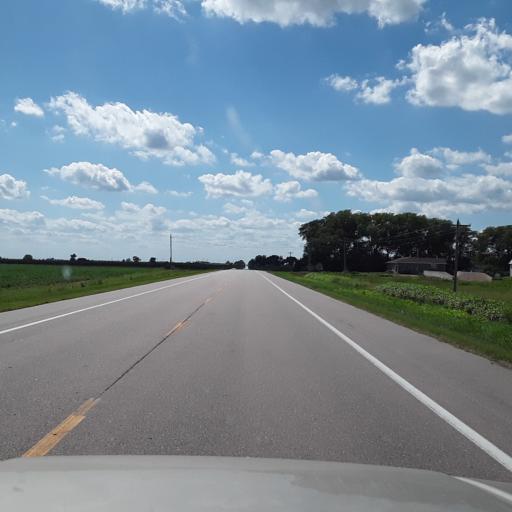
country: US
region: Nebraska
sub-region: Merrick County
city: Central City
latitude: 41.1910
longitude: -97.9891
